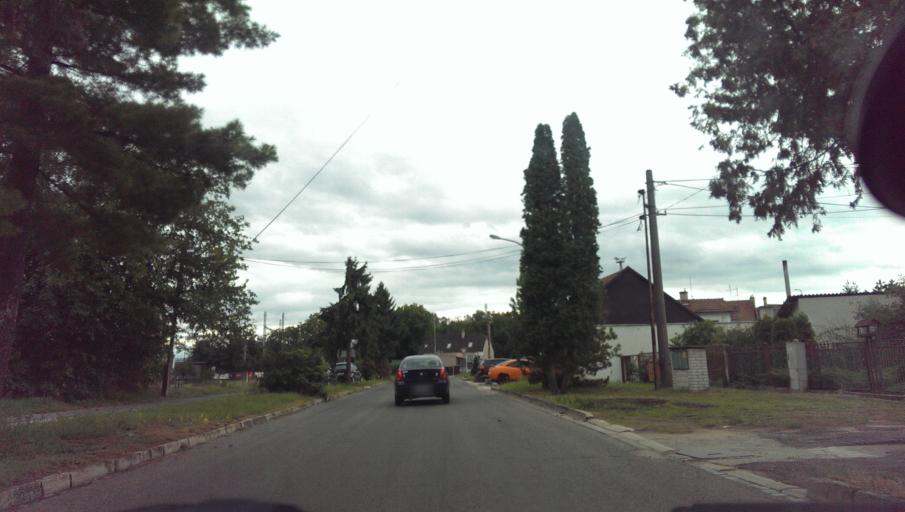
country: CZ
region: South Moravian
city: Moravsky Pisek
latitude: 48.9804
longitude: 17.3150
